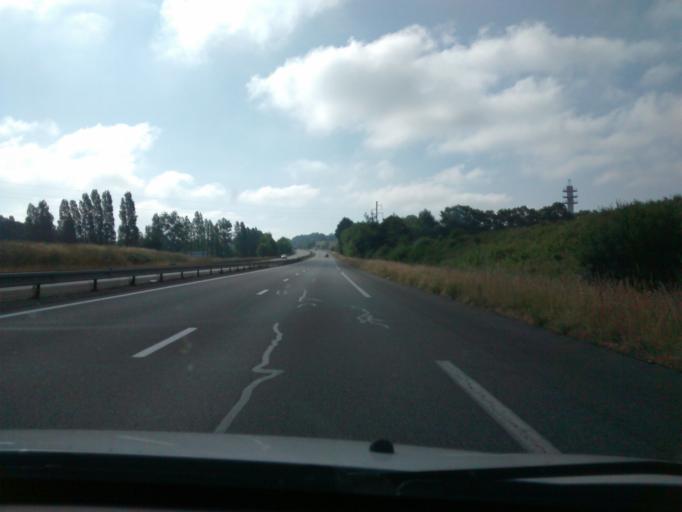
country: FR
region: Pays de la Loire
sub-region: Departement de la Mayenne
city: Saint-Pierre-la-Cour
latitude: 48.0804
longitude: -1.0042
